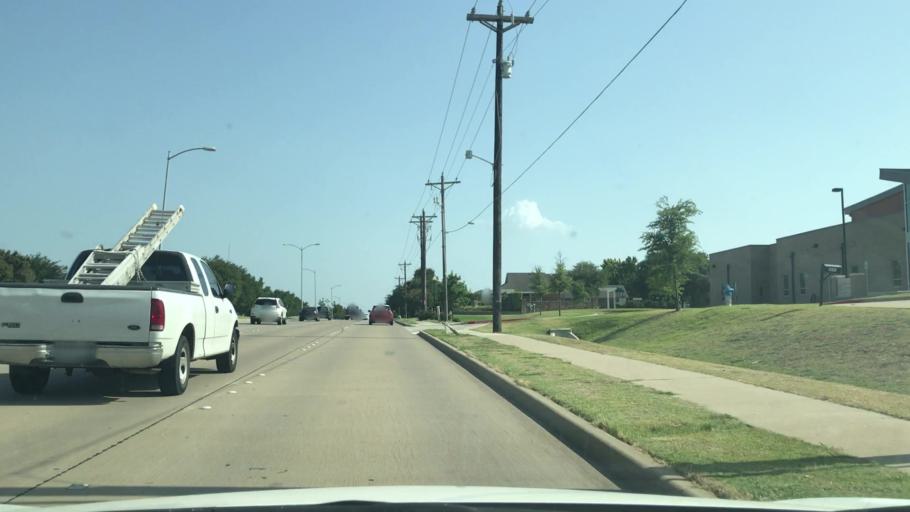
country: US
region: Texas
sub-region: Collin County
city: Allen
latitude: 33.1108
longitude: -96.7509
